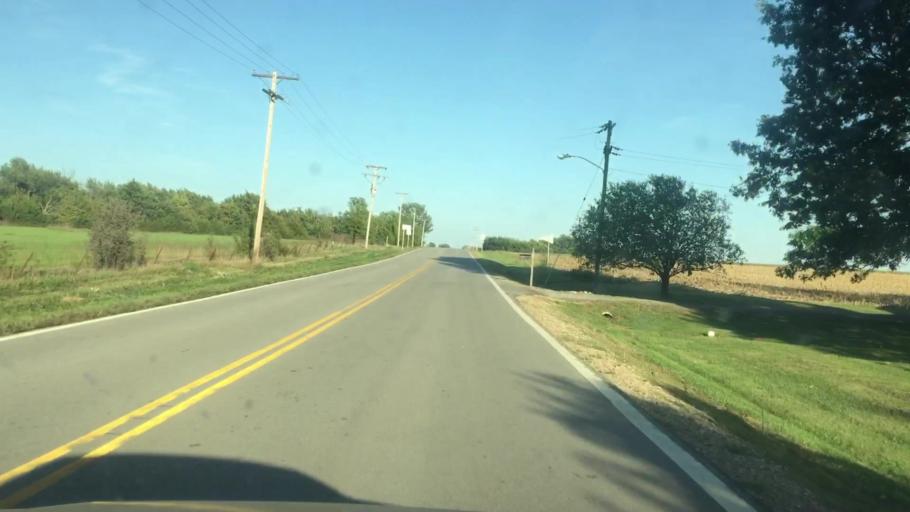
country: US
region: Kansas
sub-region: Brown County
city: Horton
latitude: 39.5876
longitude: -95.6099
